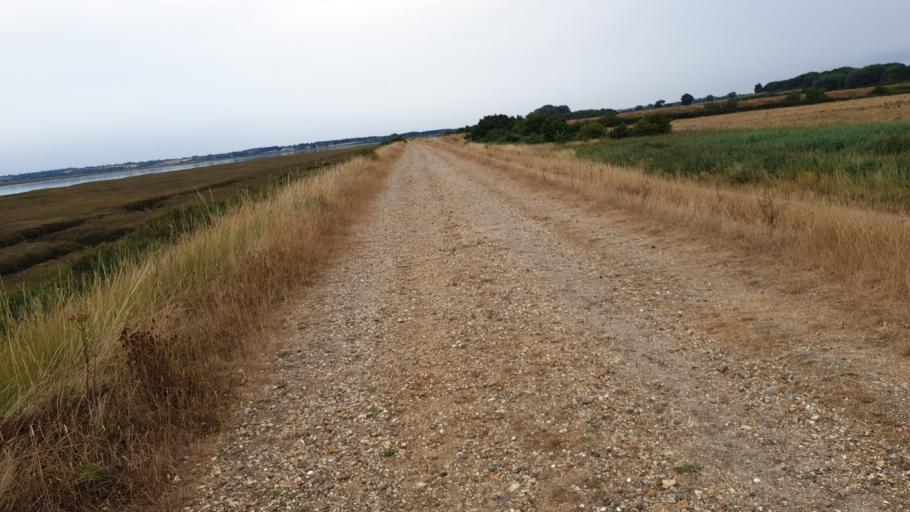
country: GB
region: England
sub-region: Essex
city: Brightlingsea
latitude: 51.8140
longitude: 0.9993
